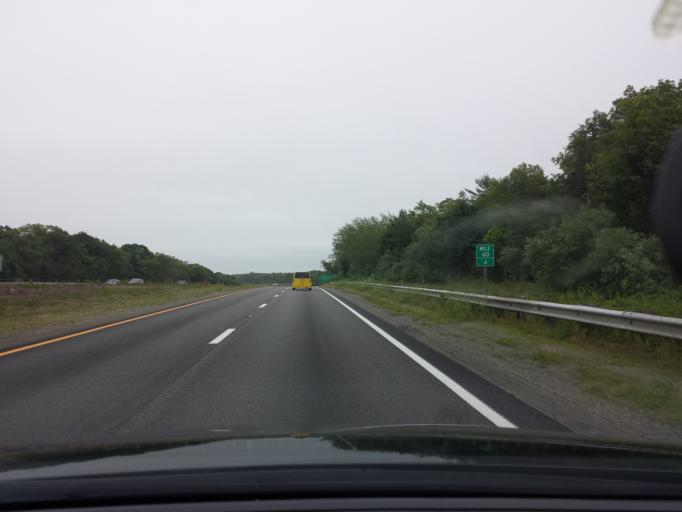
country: US
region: Massachusetts
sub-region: Barnstable County
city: East Sandwich
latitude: 41.7328
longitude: -70.4626
